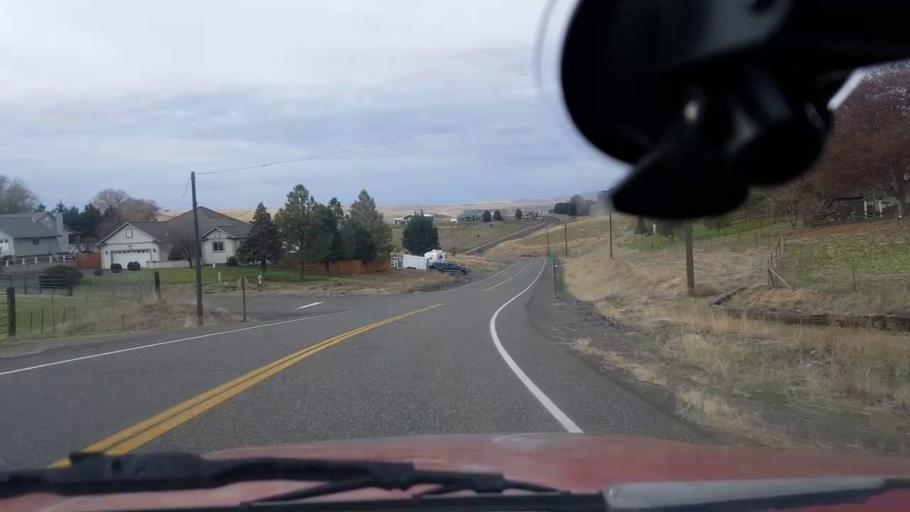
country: US
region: Washington
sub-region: Asotin County
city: Clarkston Heights-Vineland
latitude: 46.4018
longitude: -117.0844
